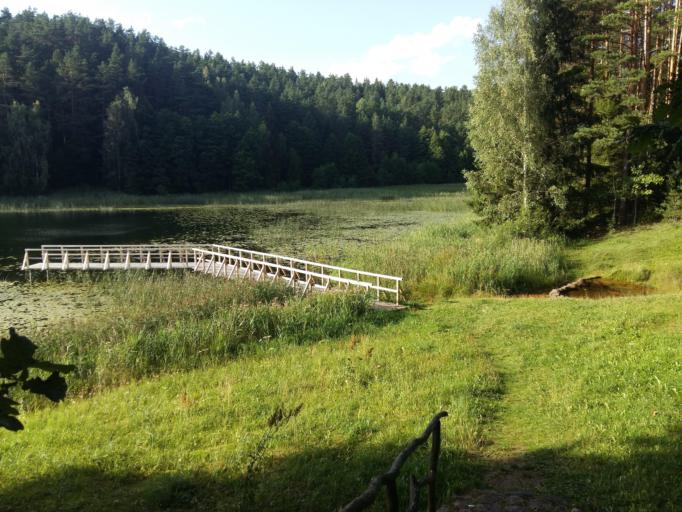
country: LT
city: Svencionys
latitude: 55.1626
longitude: 26.2476
